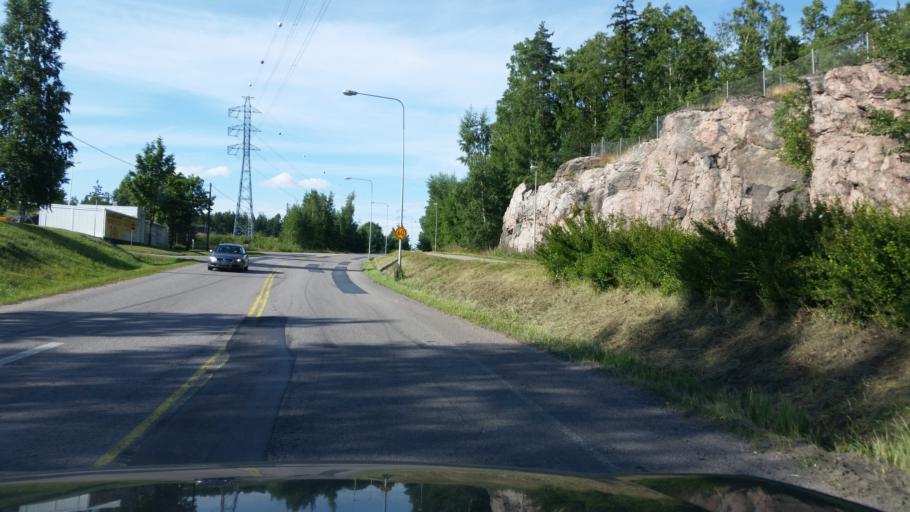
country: FI
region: Uusimaa
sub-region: Helsinki
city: Vantaa
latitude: 60.3080
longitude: 24.9993
